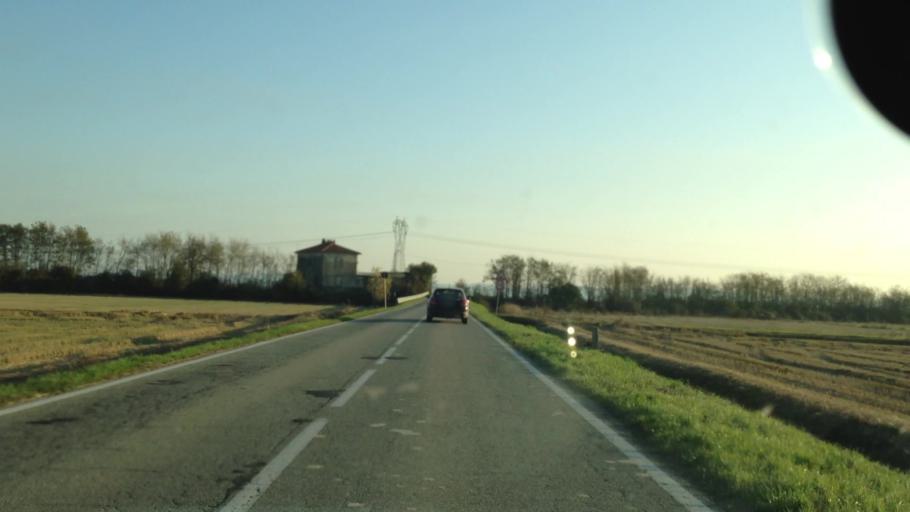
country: IT
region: Piedmont
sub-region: Provincia di Vercelli
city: Lamporo
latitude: 45.2476
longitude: 8.0895
